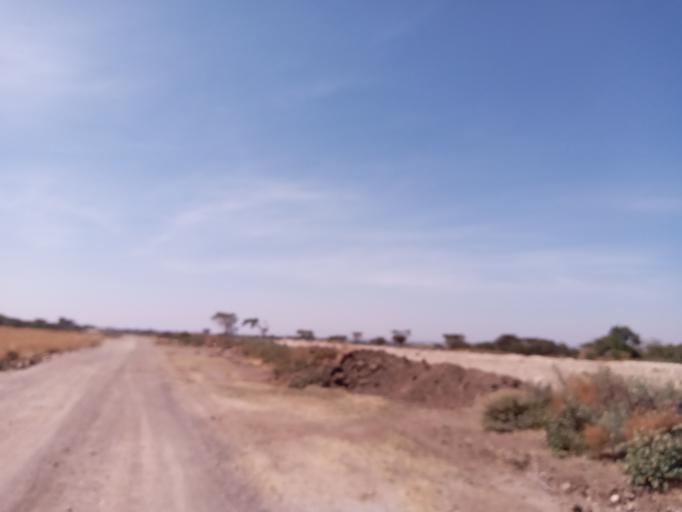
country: ET
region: Oromiya
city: Shashemene
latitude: 7.3852
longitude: 38.6501
